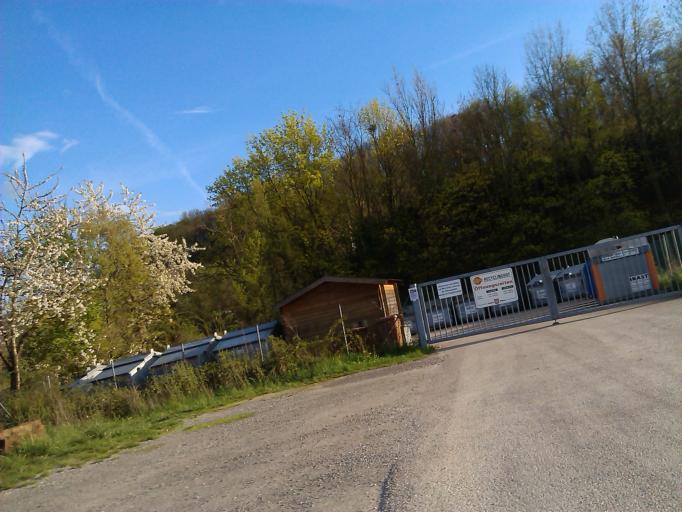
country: DE
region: Baden-Wuerttemberg
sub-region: Regierungsbezirk Stuttgart
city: Bad Wimpfen
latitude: 49.2305
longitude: 9.1823
